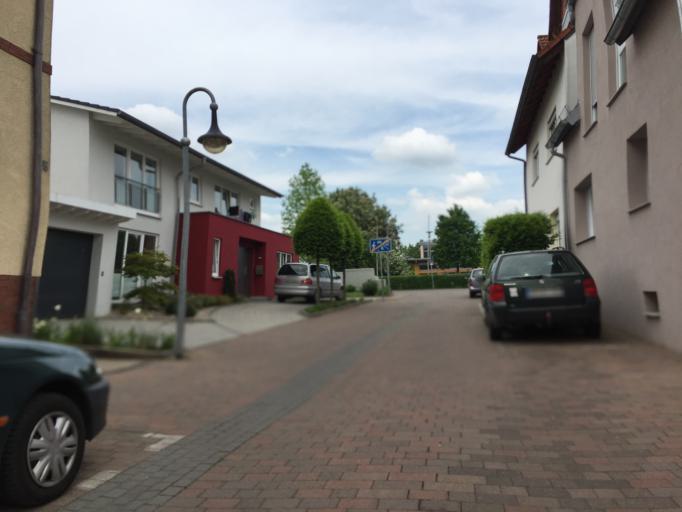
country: DE
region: Bavaria
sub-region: Regierungsbezirk Unterfranken
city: Hosbach
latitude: 50.0057
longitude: 9.2048
